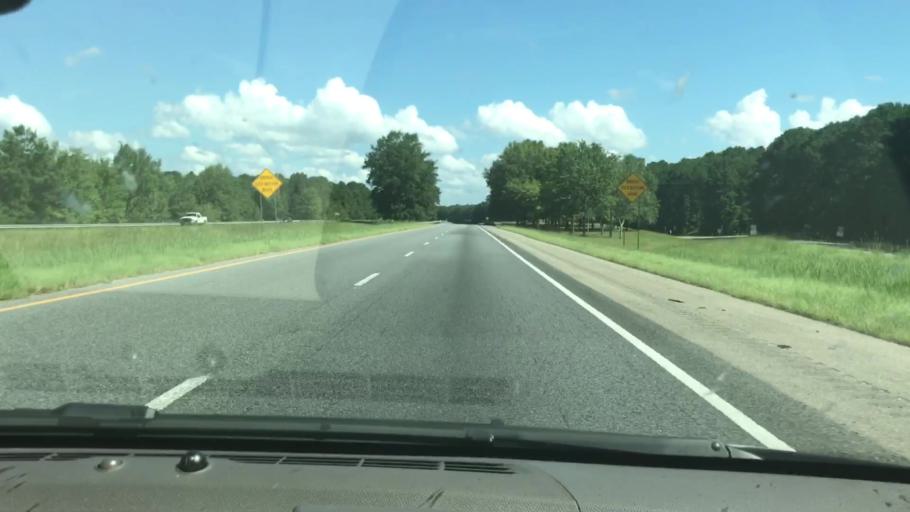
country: US
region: Georgia
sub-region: Harris County
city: Hamilton
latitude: 32.7450
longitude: -85.0181
